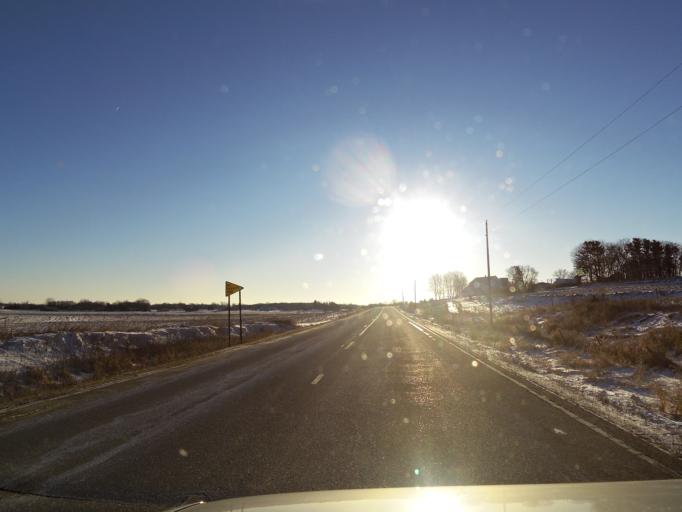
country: US
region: Minnesota
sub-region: Scott County
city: Jordan
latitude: 44.6577
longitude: -93.5281
